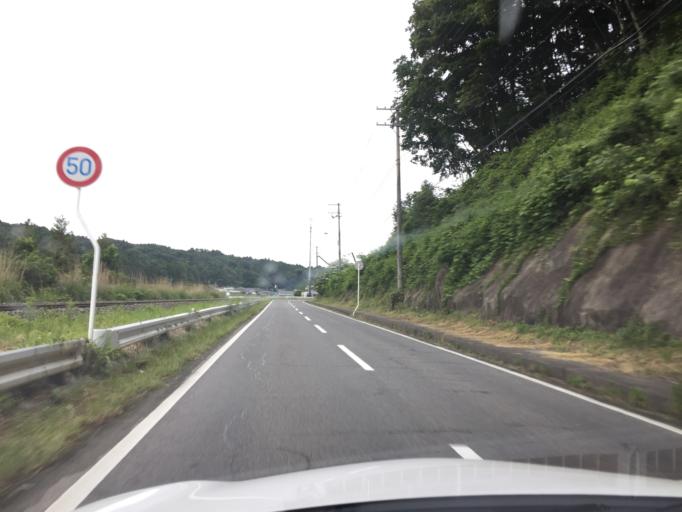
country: JP
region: Fukushima
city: Funehikimachi-funehiki
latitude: 37.3188
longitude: 140.6600
